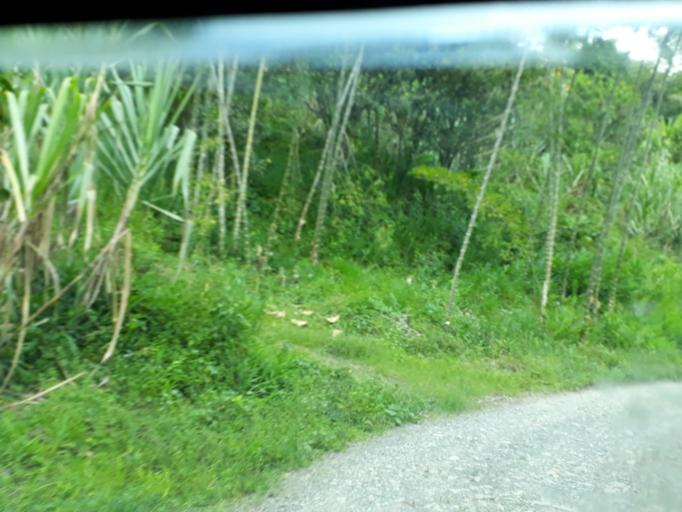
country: CO
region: Cundinamarca
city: Topaipi
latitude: 5.2830
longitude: -74.3507
